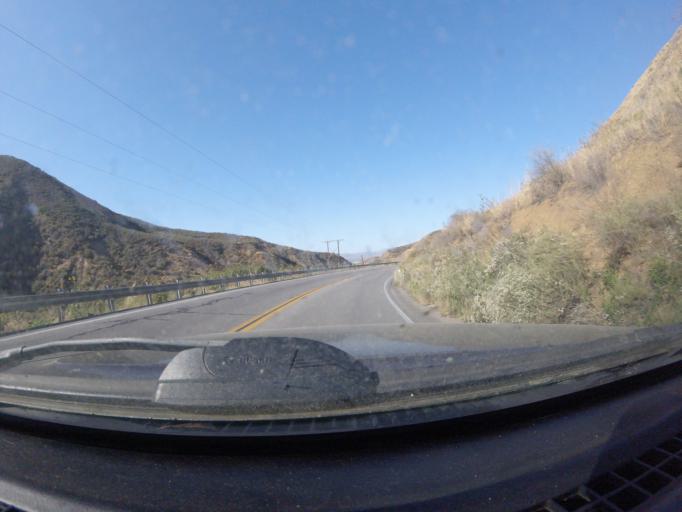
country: US
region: California
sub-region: San Bernardino County
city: Highland
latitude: 34.1561
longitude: -117.1839
